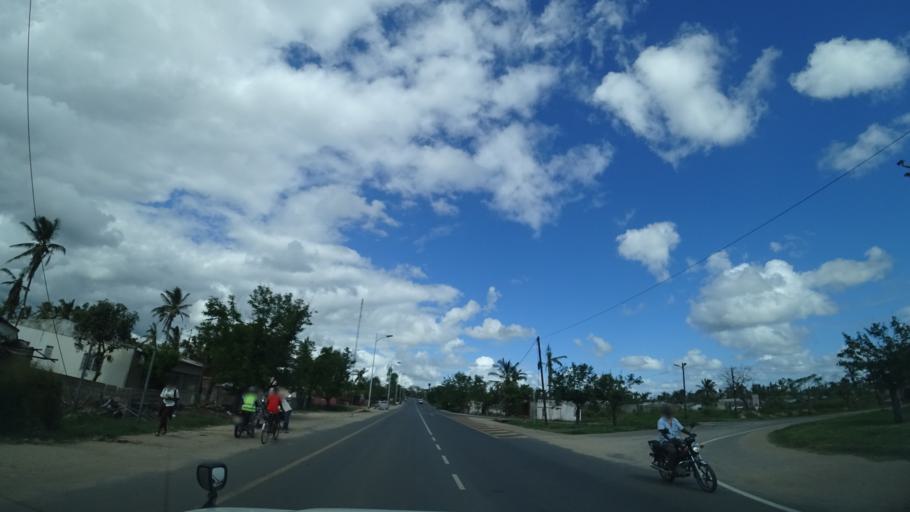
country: MZ
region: Sofala
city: Dondo
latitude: -19.5301
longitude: 34.6280
